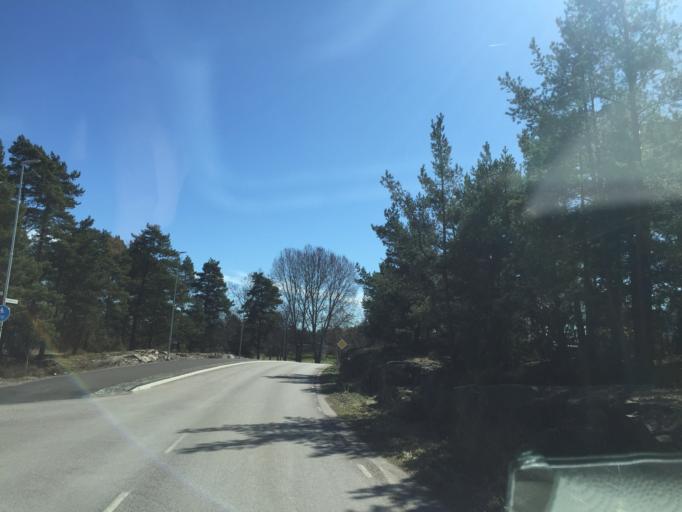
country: SE
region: Kalmar
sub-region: Oskarshamns Kommun
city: Oskarshamn
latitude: 57.2464
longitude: 16.4697
